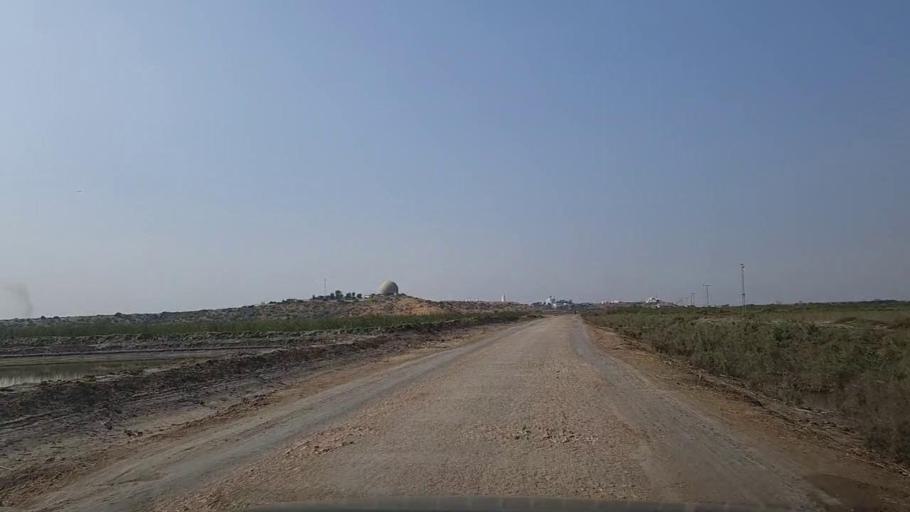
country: PK
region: Sindh
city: Chuhar Jamali
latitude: 24.5504
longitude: 67.8947
